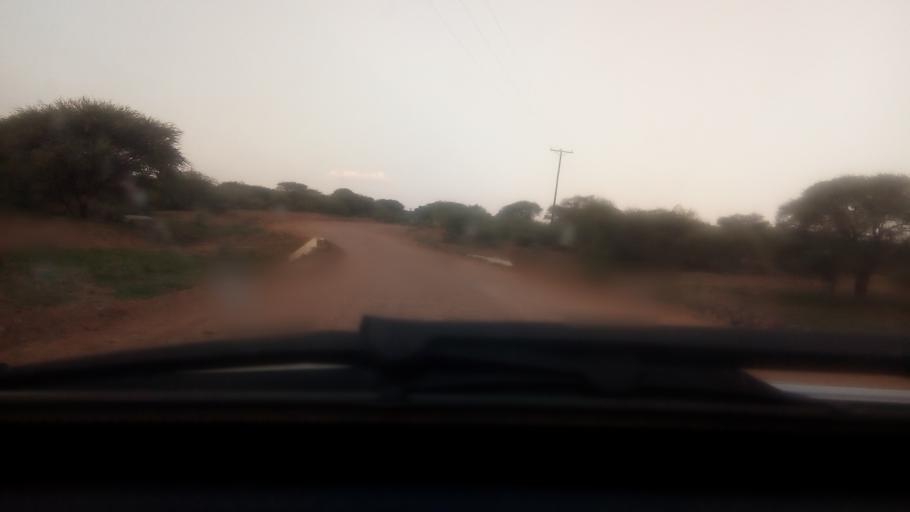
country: BW
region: Kgatleng
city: Bokaa
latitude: -24.4316
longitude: 26.0062
